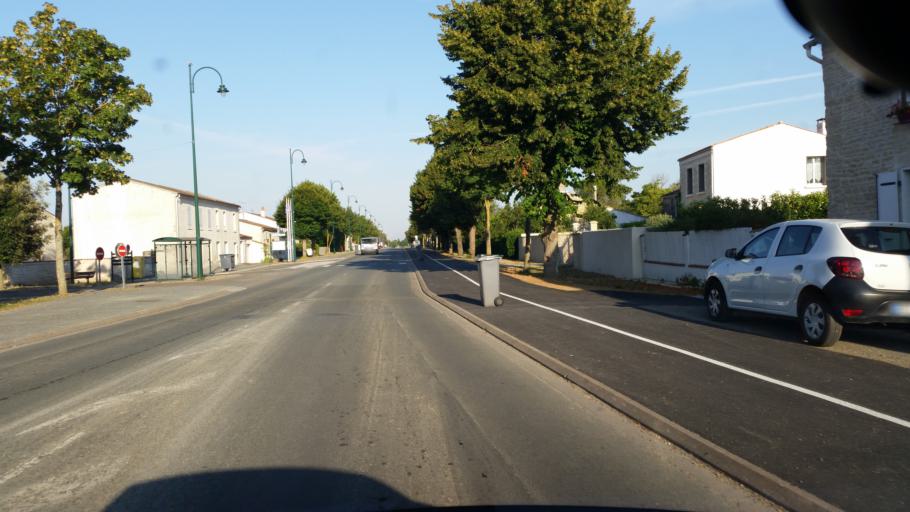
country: FR
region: Poitou-Charentes
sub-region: Departement de la Charente-Maritime
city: Saint-Jean-de-Liversay
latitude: 46.2273
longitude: -0.8635
